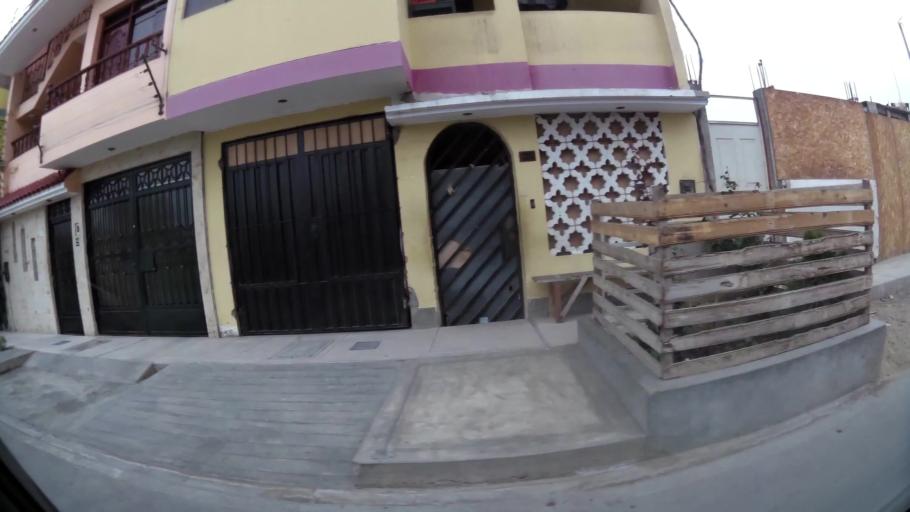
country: PE
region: Lima
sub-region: Lima
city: Independencia
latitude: -11.9761
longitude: -77.0927
